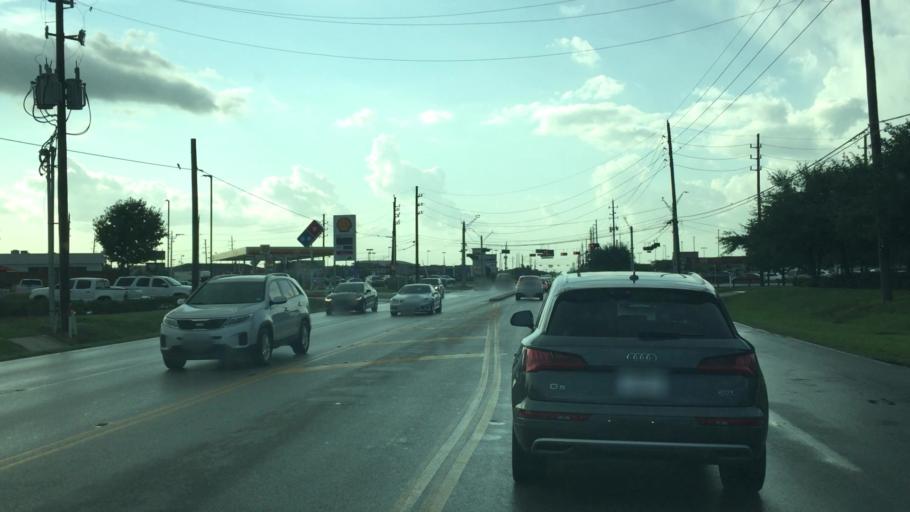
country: US
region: Texas
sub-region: Montgomery County
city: The Woodlands
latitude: 30.0730
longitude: -95.5122
